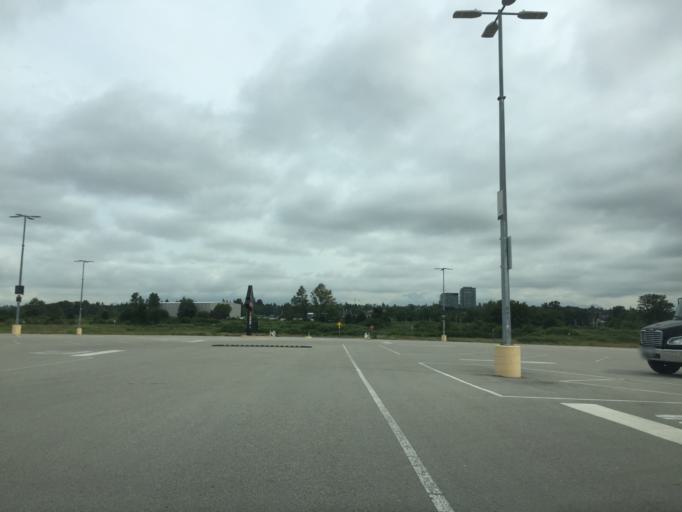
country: CA
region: British Columbia
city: Richmond
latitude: 49.1979
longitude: -123.1448
